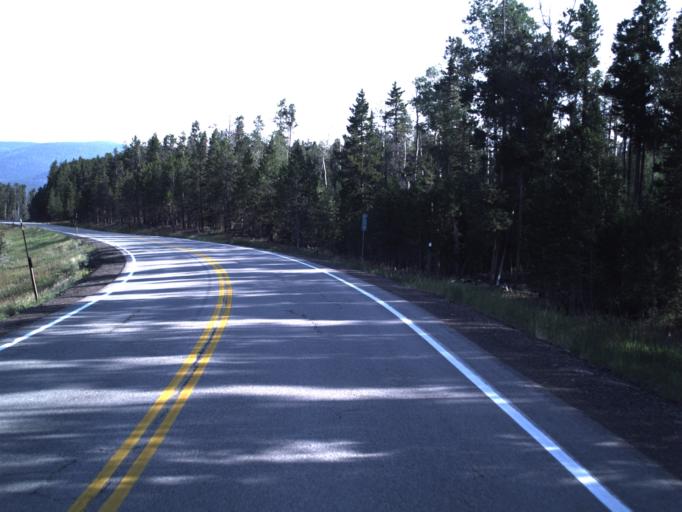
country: US
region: Utah
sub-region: Uintah County
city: Maeser
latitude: 40.7561
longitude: -109.4700
